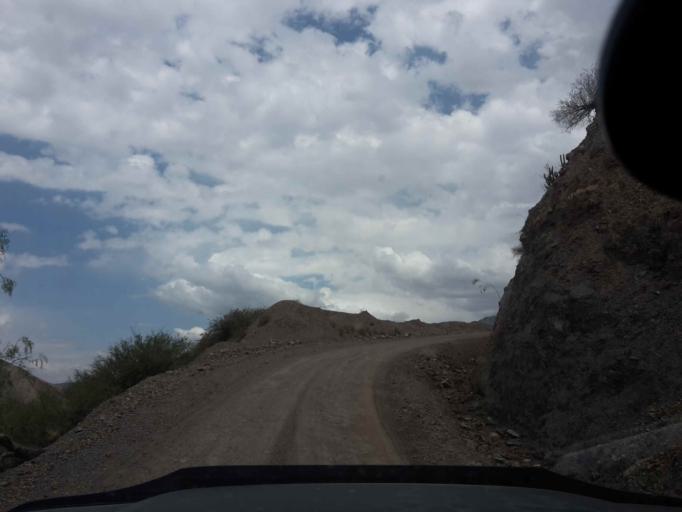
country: BO
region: Cochabamba
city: Sipe Sipe
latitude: -17.5145
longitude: -66.5999
